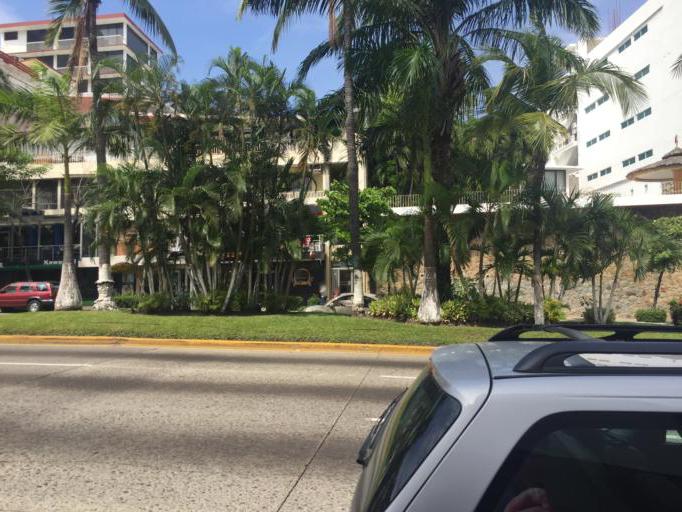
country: MX
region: Guerrero
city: Acapulco de Juarez
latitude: 16.8563
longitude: -99.8631
